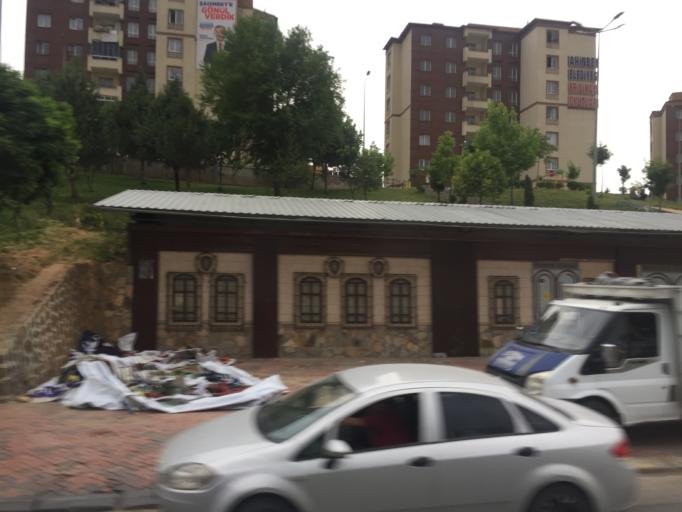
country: TR
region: Gaziantep
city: Gaziantep
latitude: 37.0548
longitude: 37.4164
